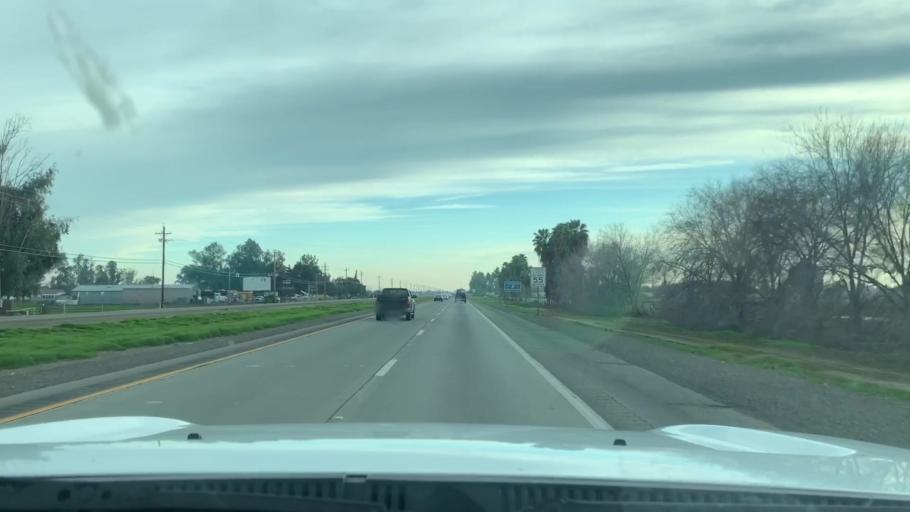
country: US
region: California
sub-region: Kings County
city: Lemoore
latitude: 36.3382
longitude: -119.8083
